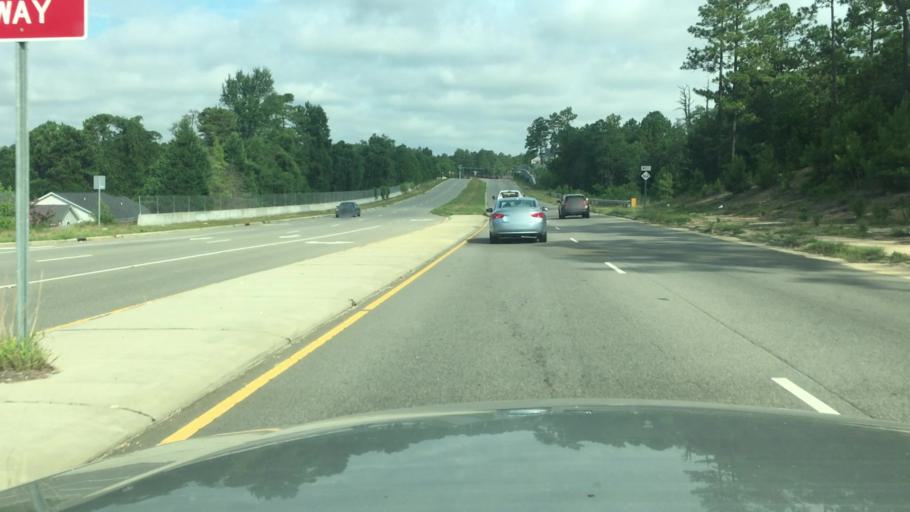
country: US
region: North Carolina
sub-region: Cumberland County
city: Hope Mills
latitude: 34.9706
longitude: -78.9159
